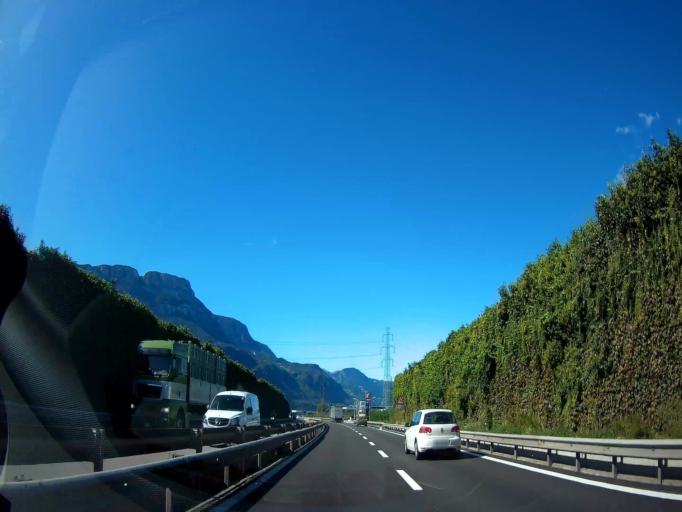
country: IT
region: Trentino-Alto Adige
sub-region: Bolzano
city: Cornaiano
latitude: 46.4836
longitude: 11.2962
